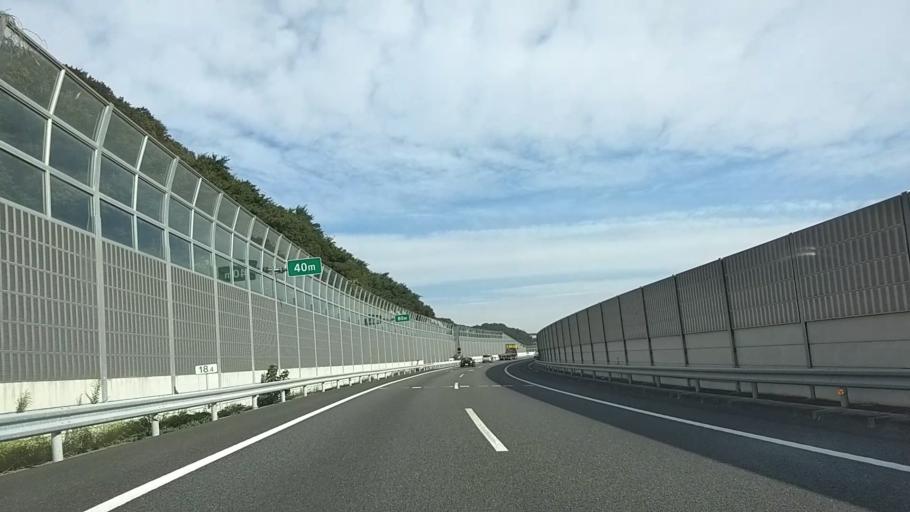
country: JP
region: Kanagawa
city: Zama
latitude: 35.4995
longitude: 139.3657
